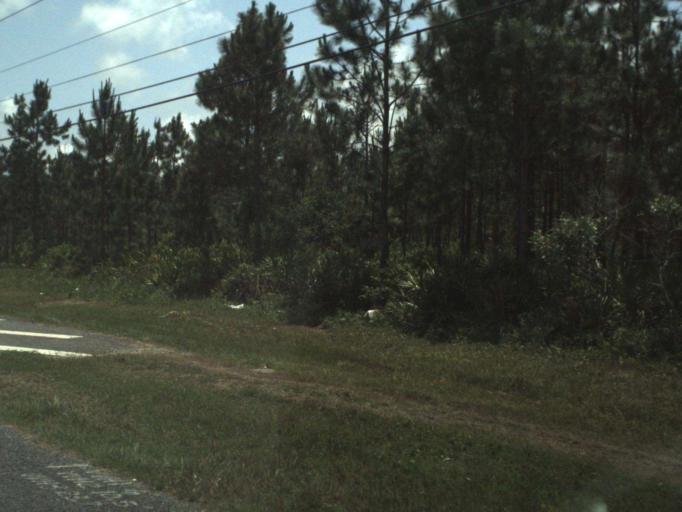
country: US
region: Florida
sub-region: Volusia County
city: Ormond-by-the-Sea
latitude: 29.3238
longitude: -81.1149
